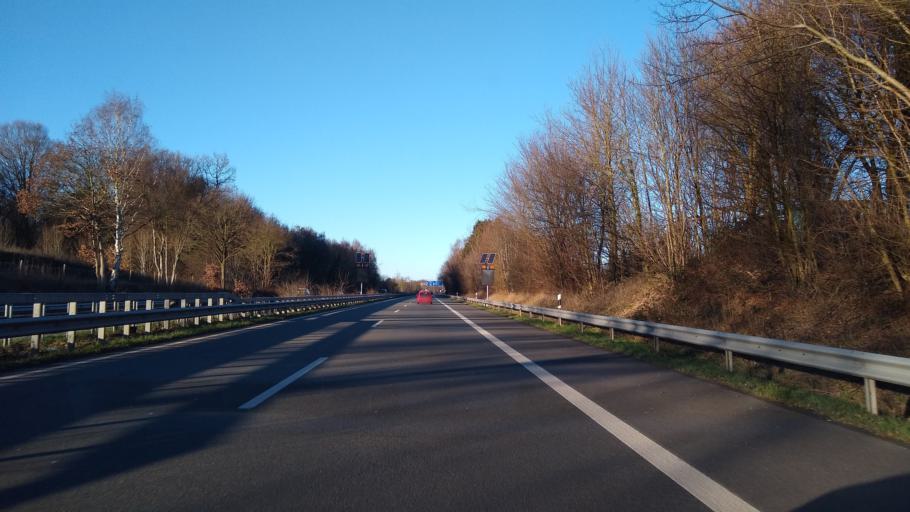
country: DE
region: Lower Saxony
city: Oldenburg
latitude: 53.1925
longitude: 8.2236
